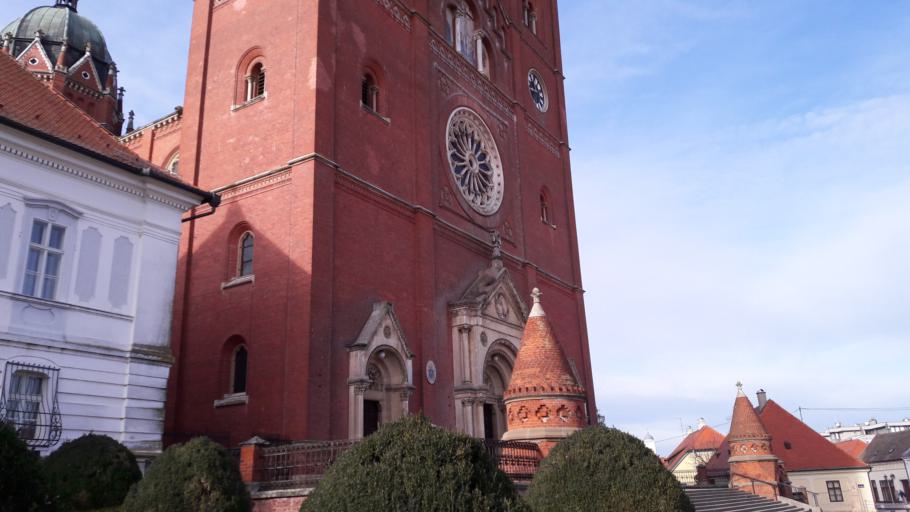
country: HR
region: Osjecko-Baranjska
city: Piskorevci
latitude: 45.3075
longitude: 18.4117
